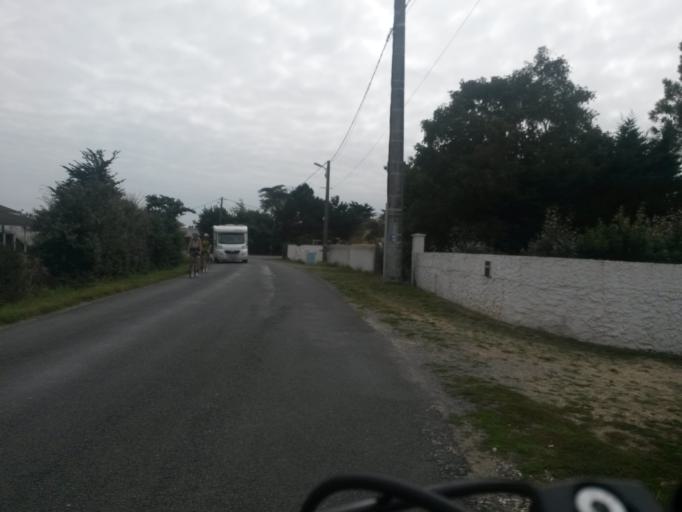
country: FR
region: Poitou-Charentes
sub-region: Departement de la Charente-Maritime
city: Saint-Denis-d'Oleron
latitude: 46.0171
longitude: -1.3927
